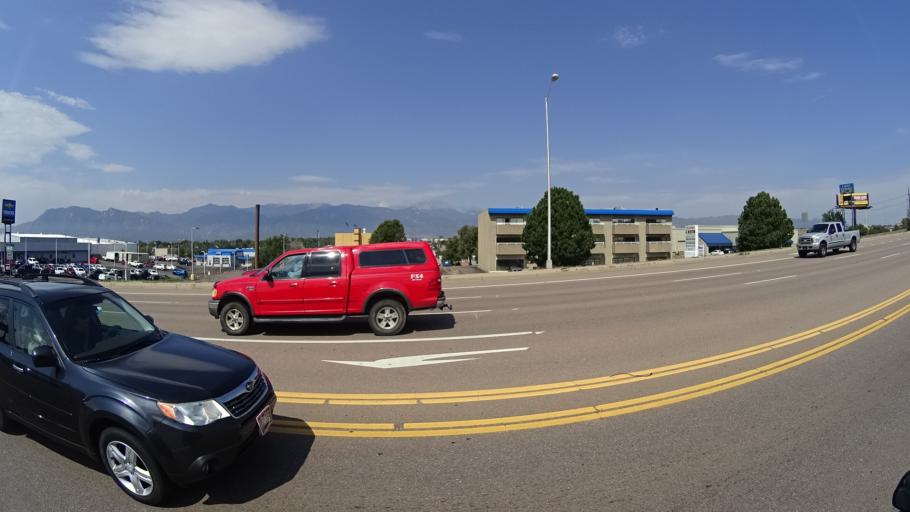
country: US
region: Colorado
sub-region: El Paso County
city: Cimarron Hills
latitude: 38.8378
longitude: -104.7572
